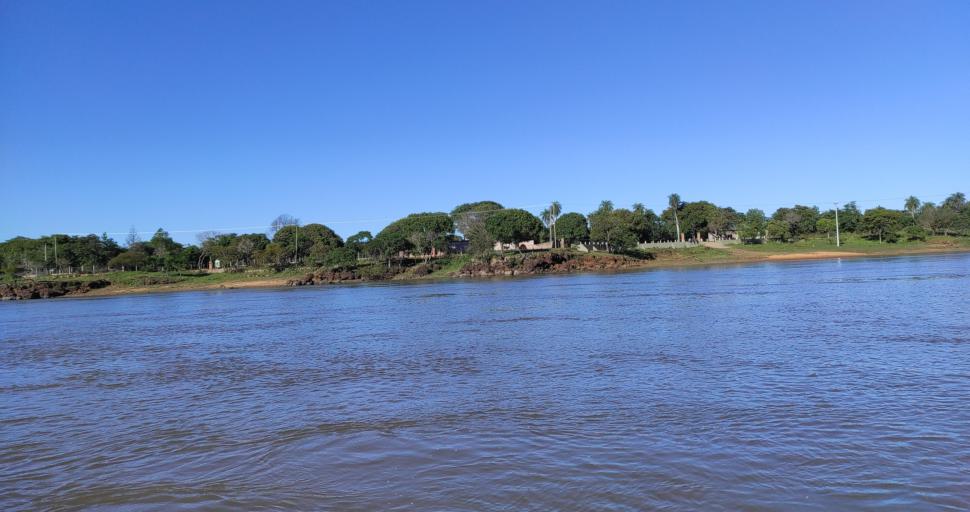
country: AR
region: Corrientes
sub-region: Departamento de Itati
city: Itati
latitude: -27.2641
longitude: -58.2568
